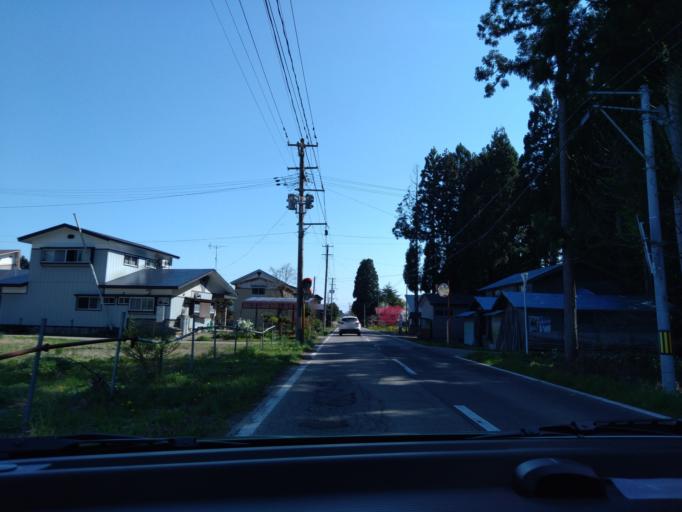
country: JP
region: Akita
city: Kakunodatemachi
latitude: 39.5478
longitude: 140.5858
